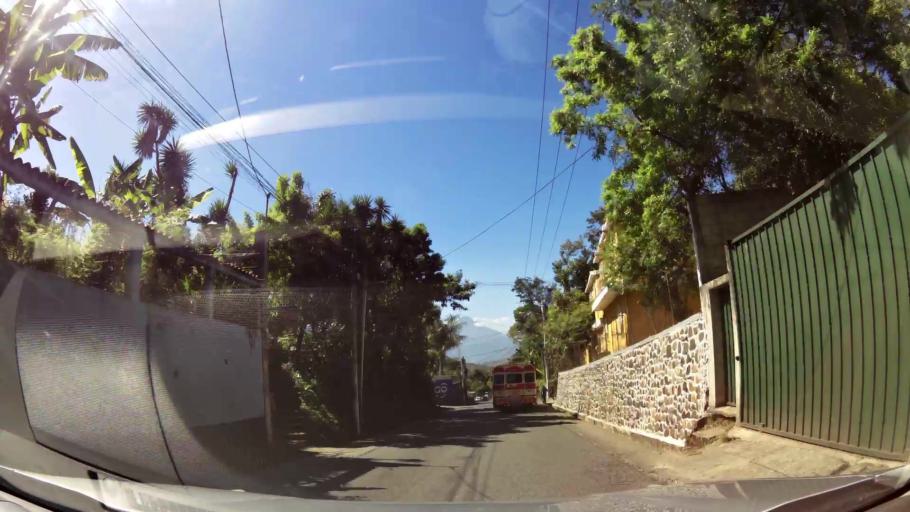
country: GT
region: Guatemala
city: Villa Canales
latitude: 14.4872
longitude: -90.5245
